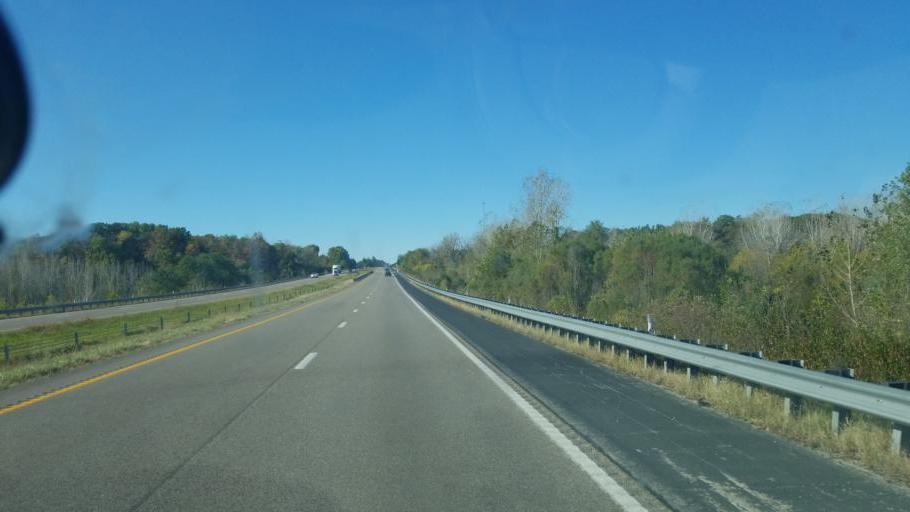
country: US
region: Missouri
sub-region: Cooper County
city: Boonville
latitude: 38.9467
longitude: -92.5658
